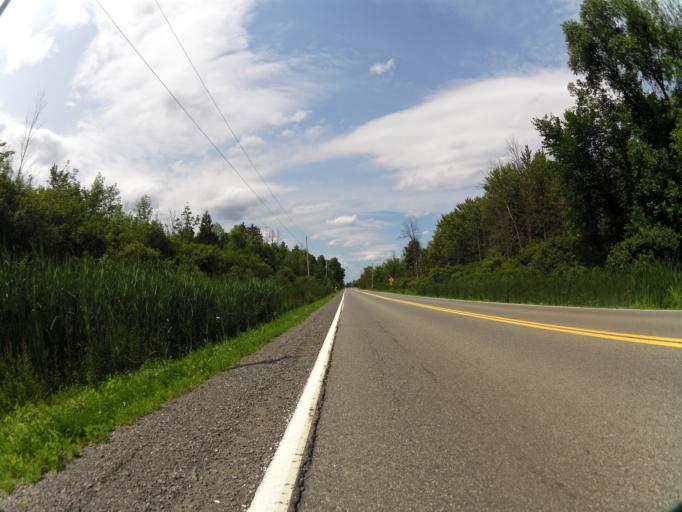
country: CA
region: Ontario
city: Ottawa
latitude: 45.2256
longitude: -75.6059
